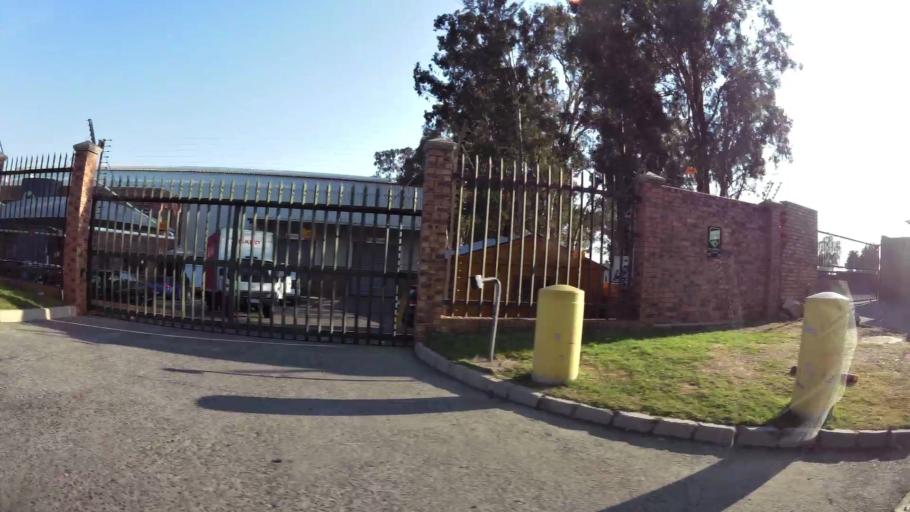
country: ZA
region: Gauteng
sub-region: City of Johannesburg Metropolitan Municipality
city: Modderfontein
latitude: -26.1576
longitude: 28.1849
